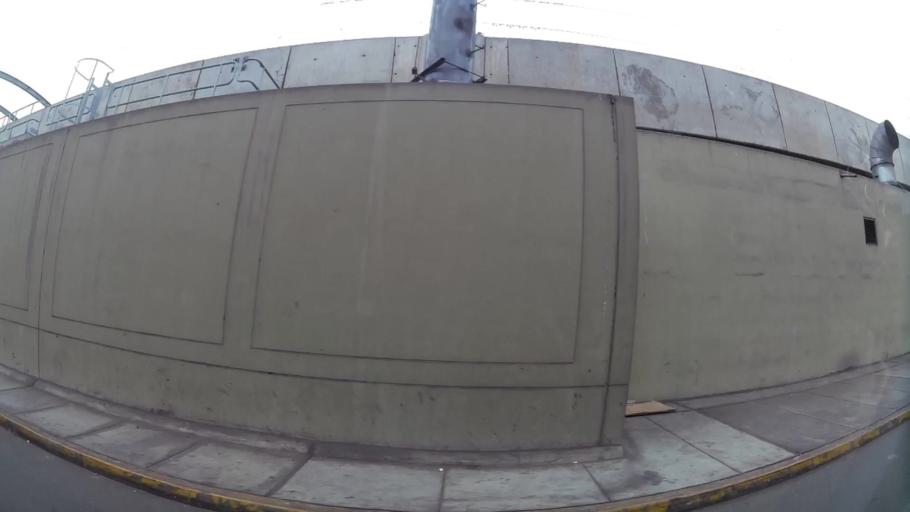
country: PE
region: Lima
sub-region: Lima
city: Surco
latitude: -12.1264
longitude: -77.0001
